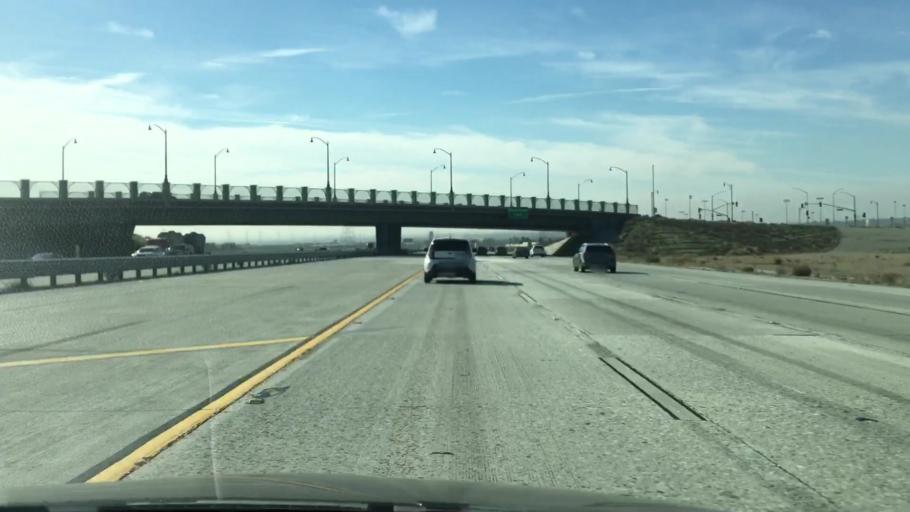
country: US
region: California
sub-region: San Bernardino County
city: Fontana
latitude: 34.1661
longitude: -117.4603
